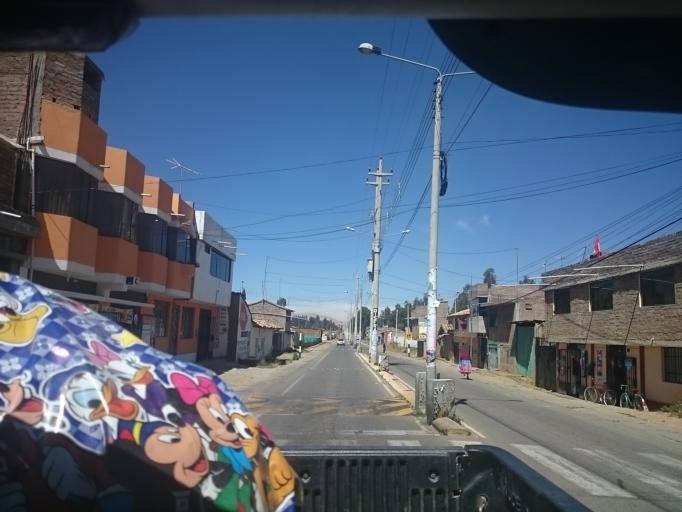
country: PE
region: Junin
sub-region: Provincia de Jauja
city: Acolla
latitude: -11.7304
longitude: -75.5455
